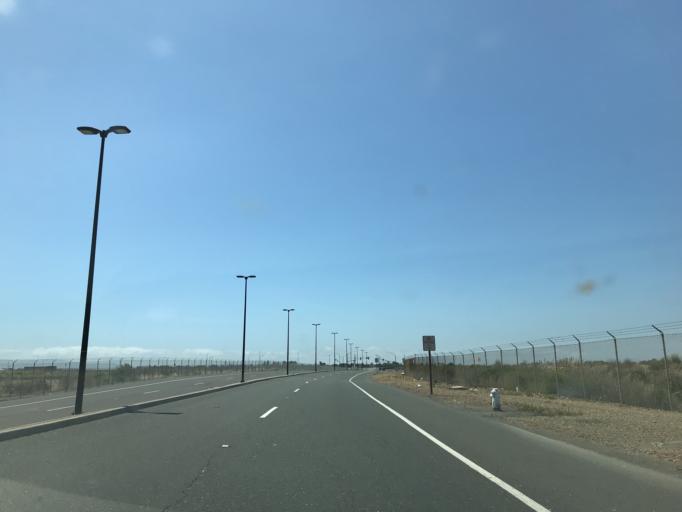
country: US
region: California
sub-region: Alameda County
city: Alameda
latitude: 37.7221
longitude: -122.2134
